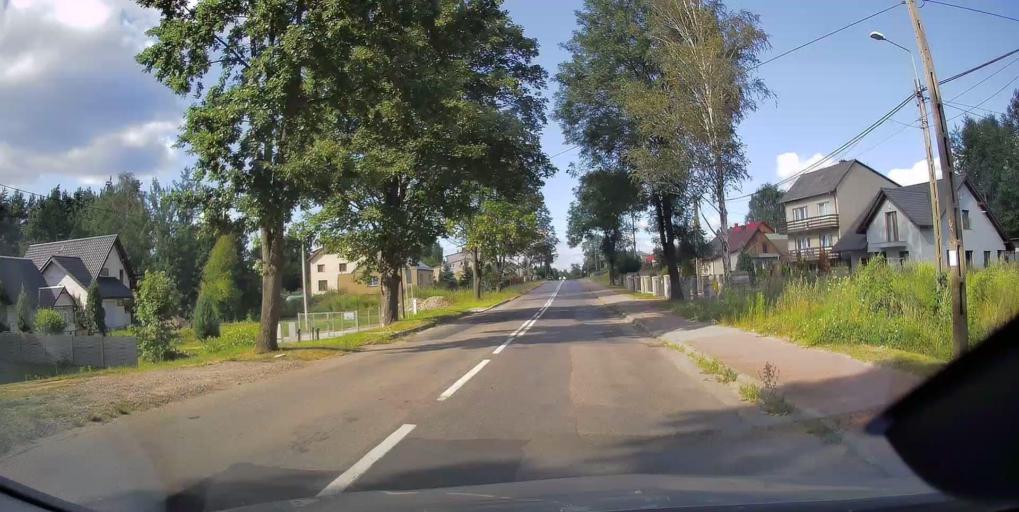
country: PL
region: Swietokrzyskie
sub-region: Powiat skarzyski
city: Suchedniow
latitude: 51.0284
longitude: 20.8377
